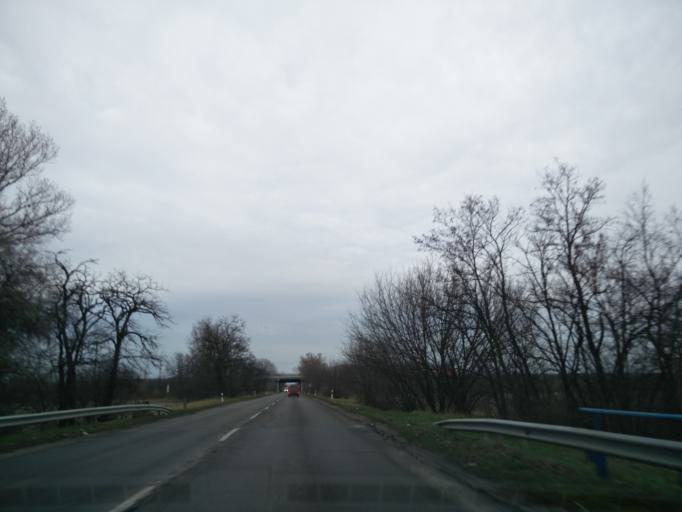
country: HU
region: Pest
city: Vecses
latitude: 47.3979
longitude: 19.3007
